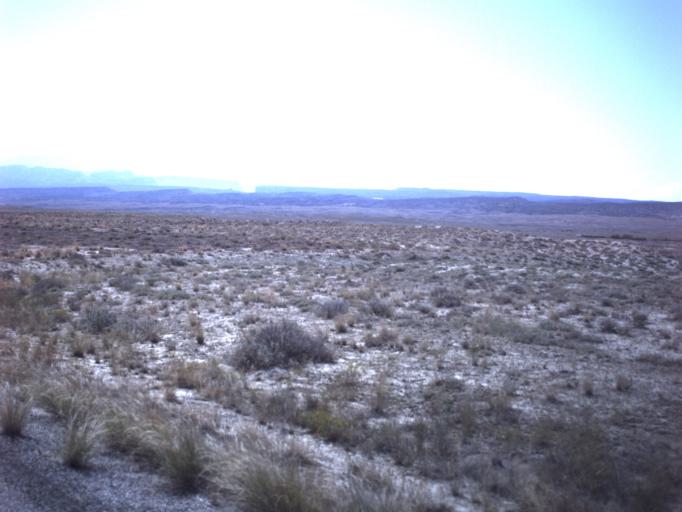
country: US
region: Utah
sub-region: Grand County
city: Moab
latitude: 38.9210
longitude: -109.3350
